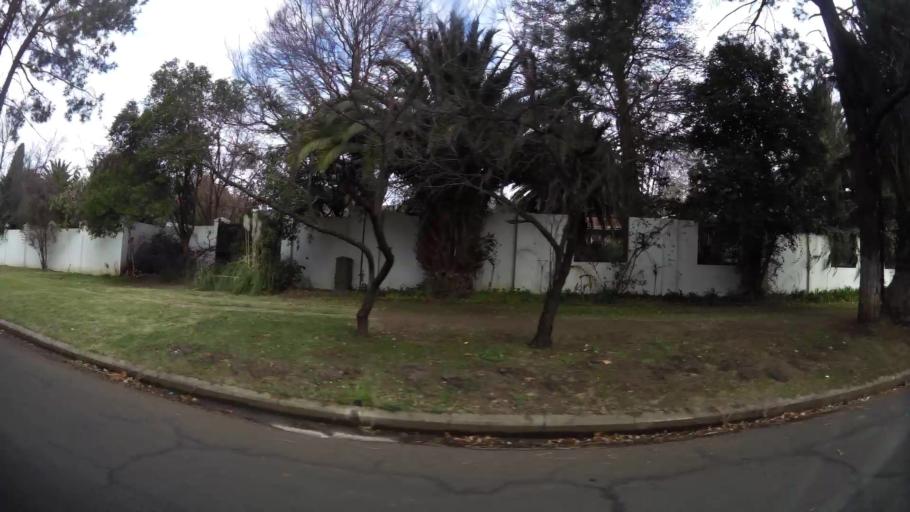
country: ZA
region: Orange Free State
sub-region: Mangaung Metropolitan Municipality
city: Bloemfontein
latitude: -29.0910
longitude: 26.2360
